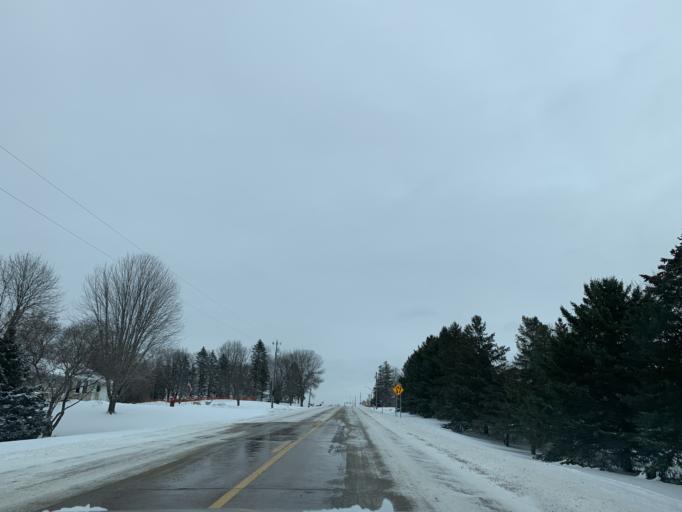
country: US
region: Minnesota
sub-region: Carver County
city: Carver
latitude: 44.7911
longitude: -93.6391
